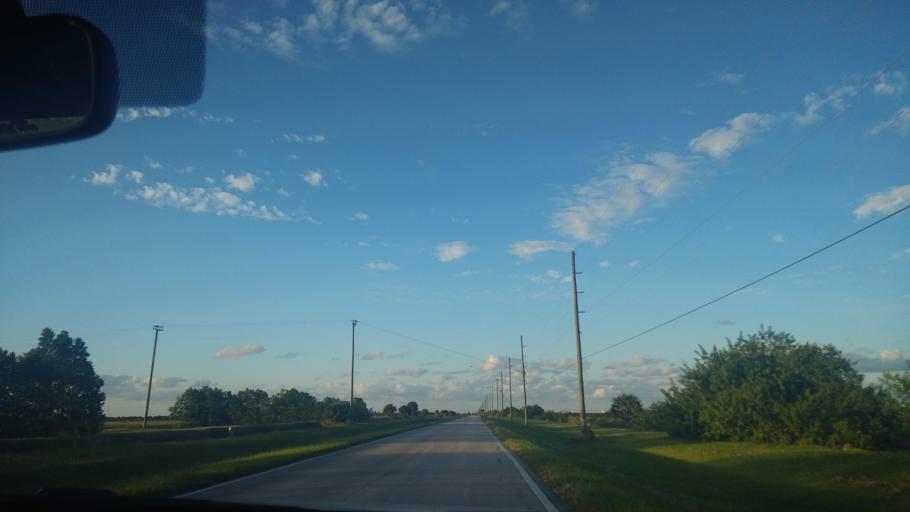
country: US
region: Florida
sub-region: Indian River County
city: Fellsmere
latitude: 27.7078
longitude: -80.6427
